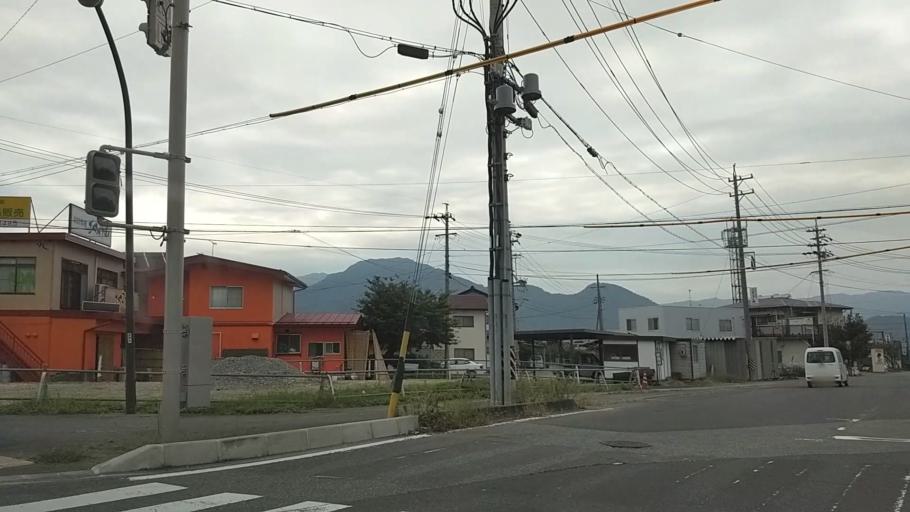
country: JP
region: Nagano
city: Nagano-shi
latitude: 36.6124
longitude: 138.2091
